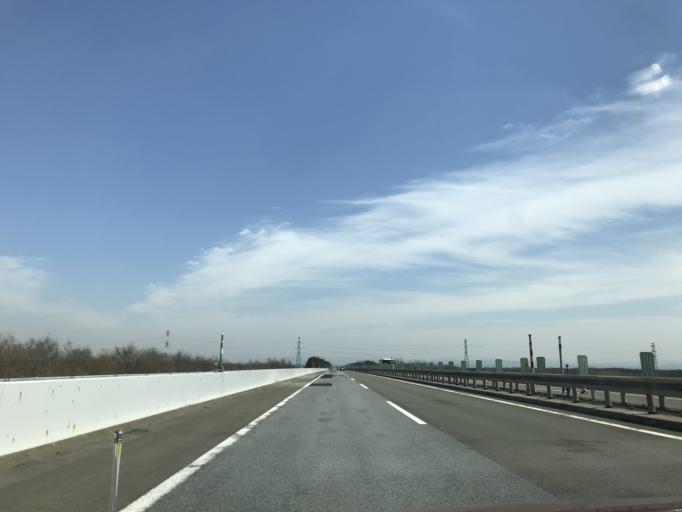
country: JP
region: Hokkaido
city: Ebetsu
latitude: 43.1152
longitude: 141.6192
